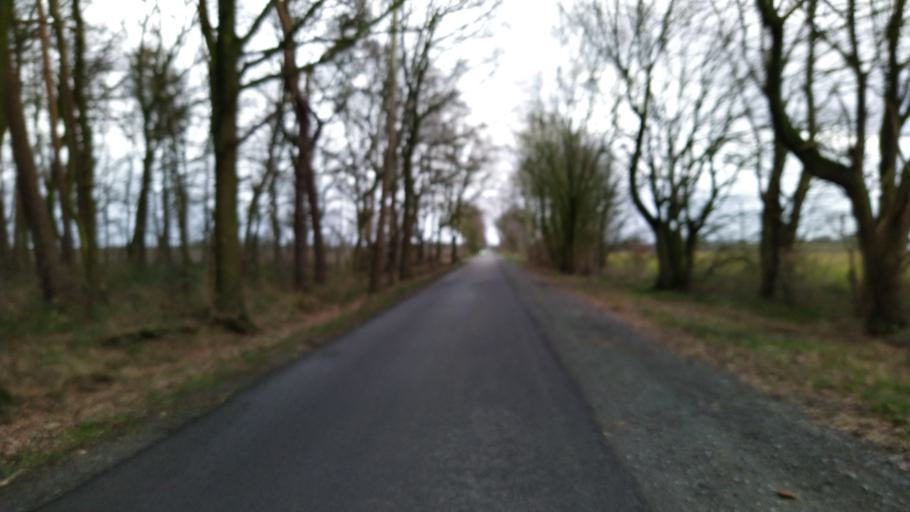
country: DE
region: Lower Saxony
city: Bargstedt
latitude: 53.4473
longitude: 9.4664
